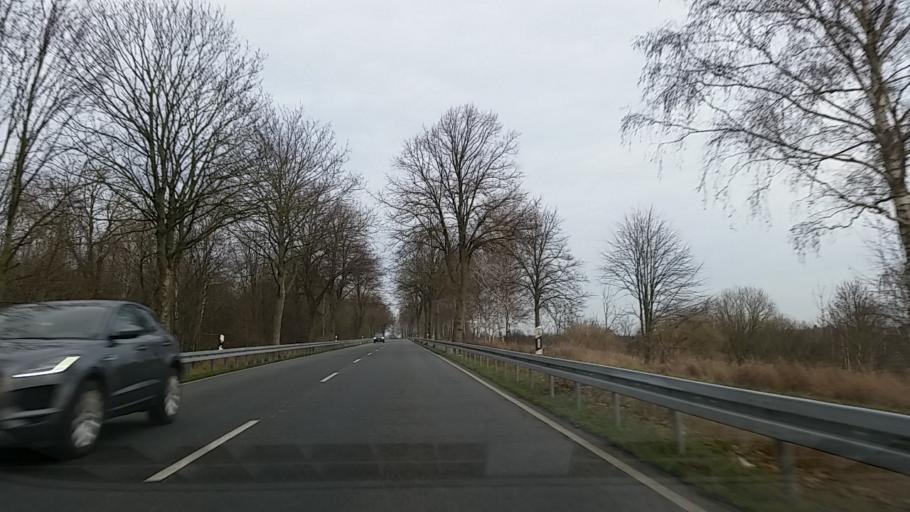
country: DE
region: Lower Saxony
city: Cramme
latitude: 52.1282
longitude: 10.4309
